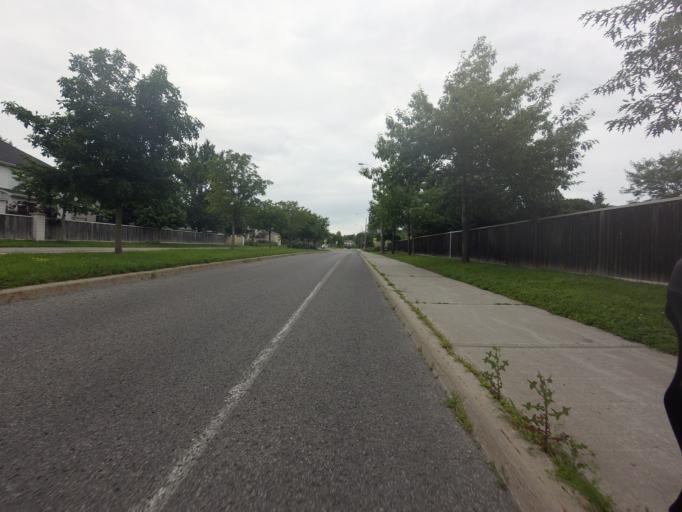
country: CA
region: Ontario
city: Ottawa
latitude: 45.2880
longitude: -75.7094
